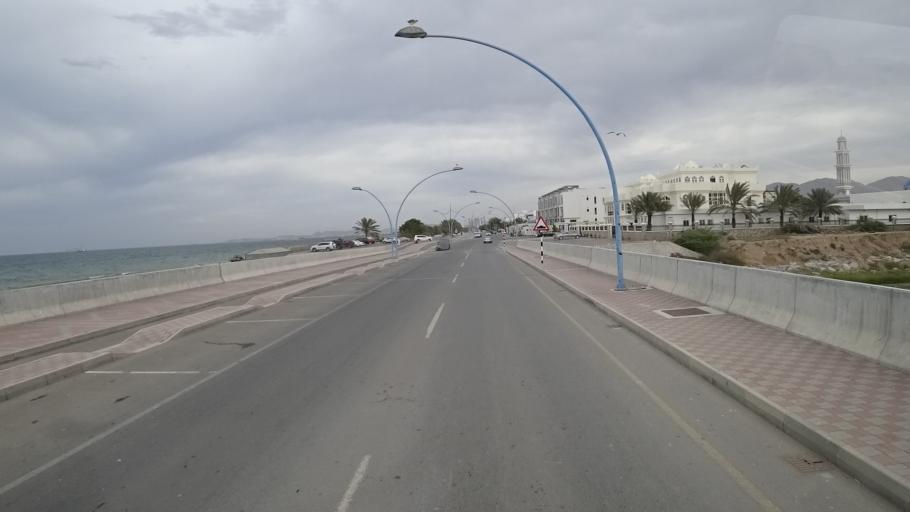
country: OM
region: Muhafazat Masqat
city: Bawshar
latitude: 23.6034
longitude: 58.3844
